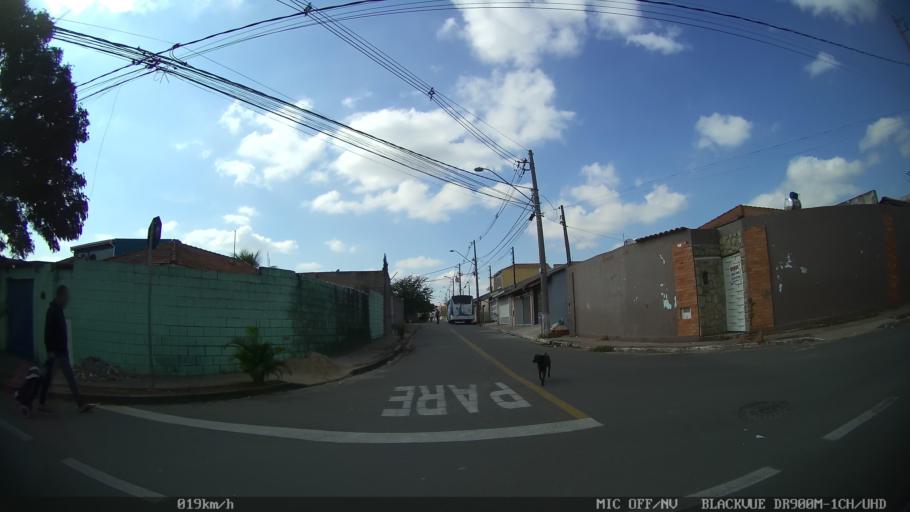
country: BR
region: Sao Paulo
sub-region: Indaiatuba
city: Indaiatuba
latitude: -22.9725
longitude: -47.1774
